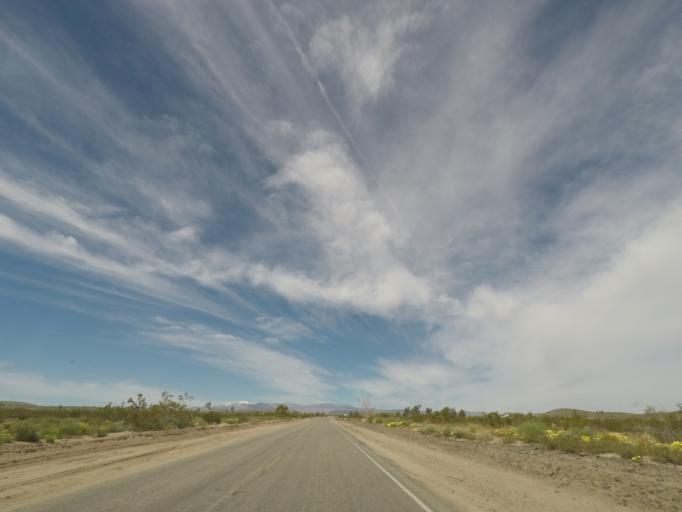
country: US
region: California
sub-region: San Bernardino County
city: Joshua Tree
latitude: 34.1929
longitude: -116.3324
